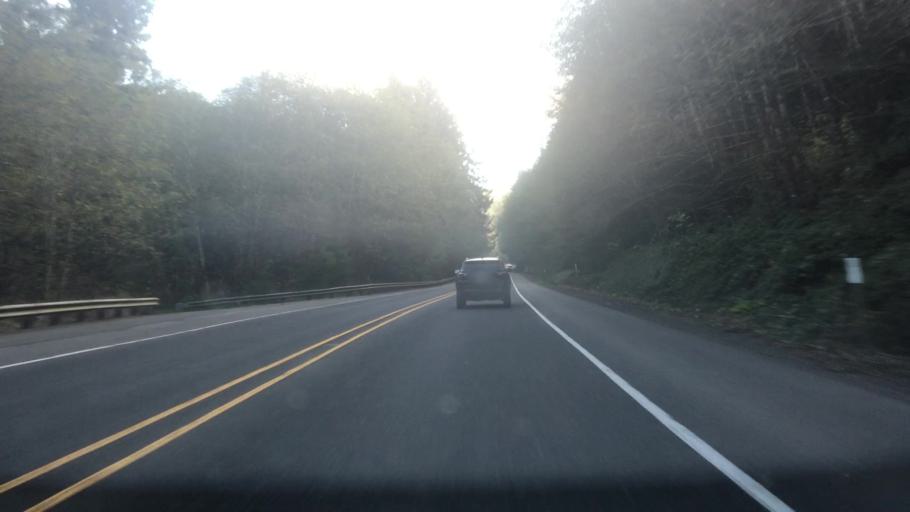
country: US
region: Oregon
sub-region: Clatsop County
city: Cannon Beach
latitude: 45.9300
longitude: -123.9281
